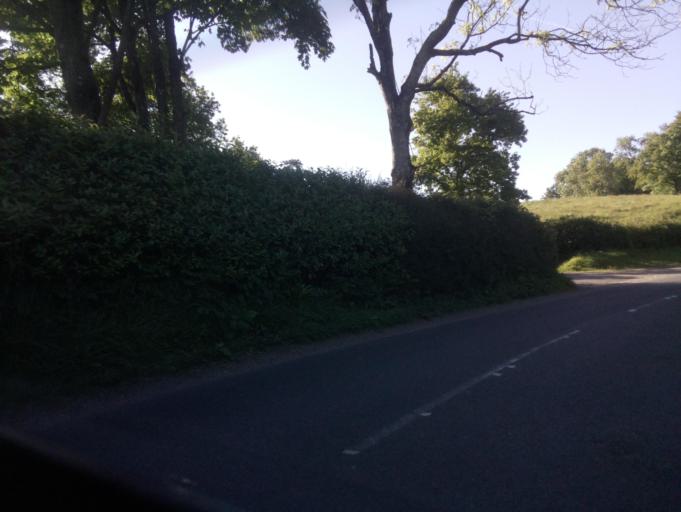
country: GB
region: England
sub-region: Somerset
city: Crewkerne
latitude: 50.8246
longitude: -2.8584
